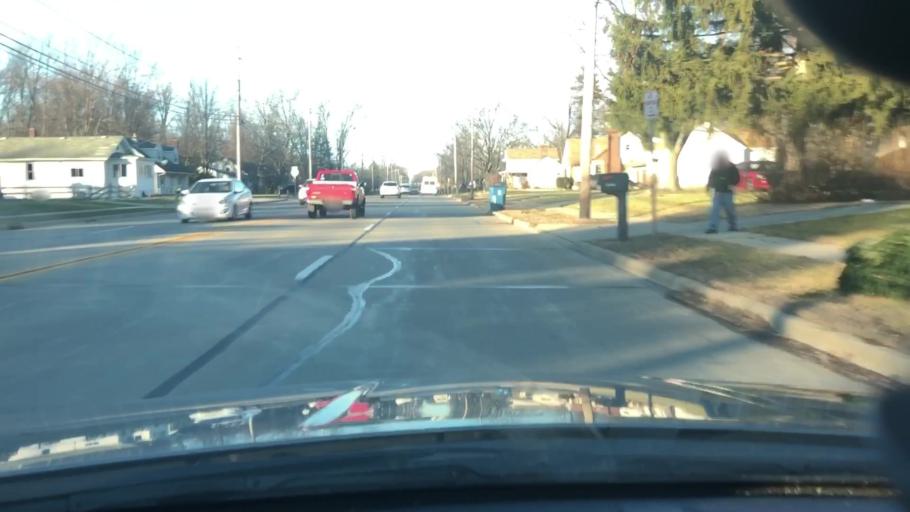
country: US
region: Ohio
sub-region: Cuyahoga County
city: North Olmsted
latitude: 41.4008
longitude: -81.9435
